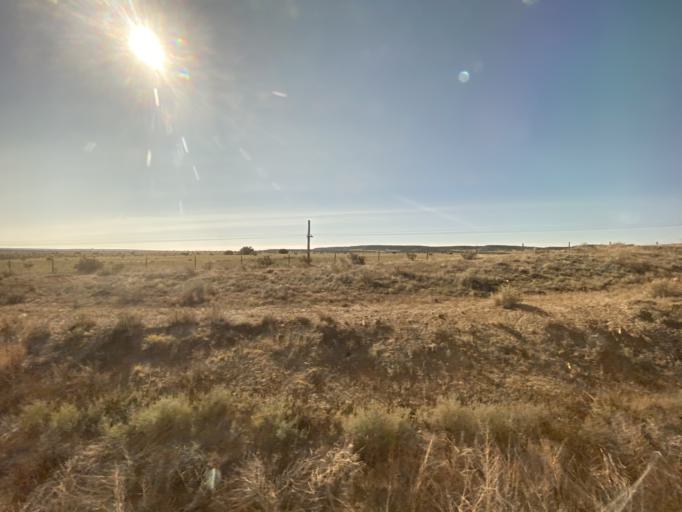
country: US
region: Colorado
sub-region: Otero County
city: Fowler
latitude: 37.5625
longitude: -104.0849
